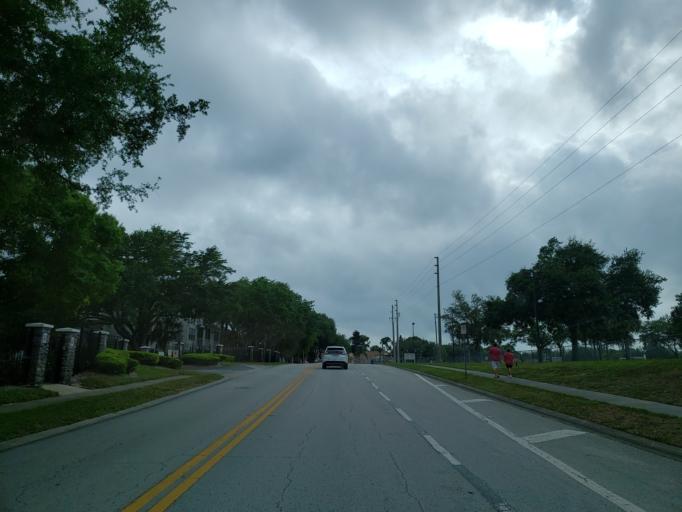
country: US
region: Florida
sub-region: Pinellas County
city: Saint George
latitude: 28.0878
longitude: -82.7256
